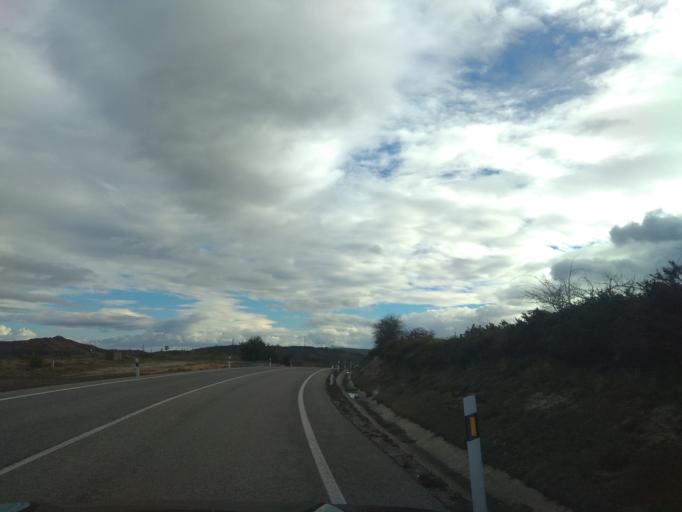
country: ES
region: Castille and Leon
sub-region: Provincia de Burgos
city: Arija
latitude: 42.9927
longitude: -3.8272
